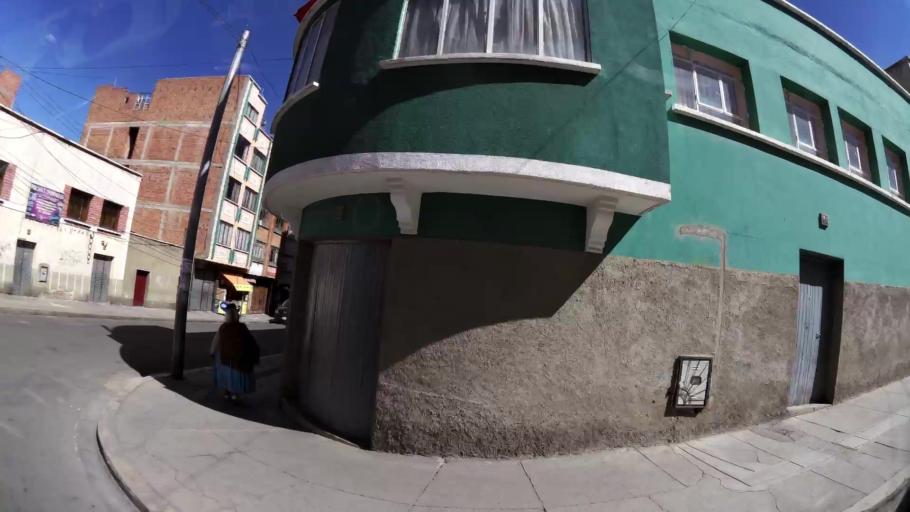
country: BO
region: La Paz
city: La Paz
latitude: -16.4926
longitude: -68.1557
